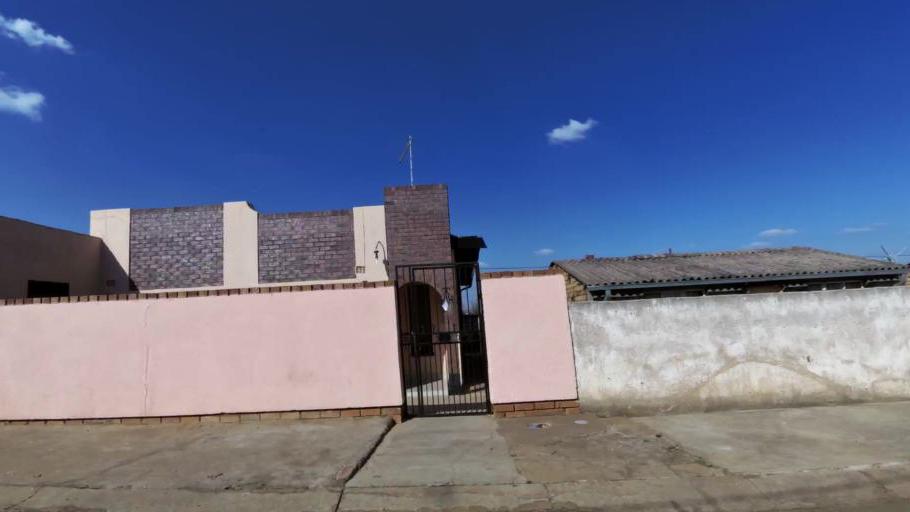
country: ZA
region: Gauteng
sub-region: City of Johannesburg Metropolitan Municipality
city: Soweto
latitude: -26.2364
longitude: 27.8733
